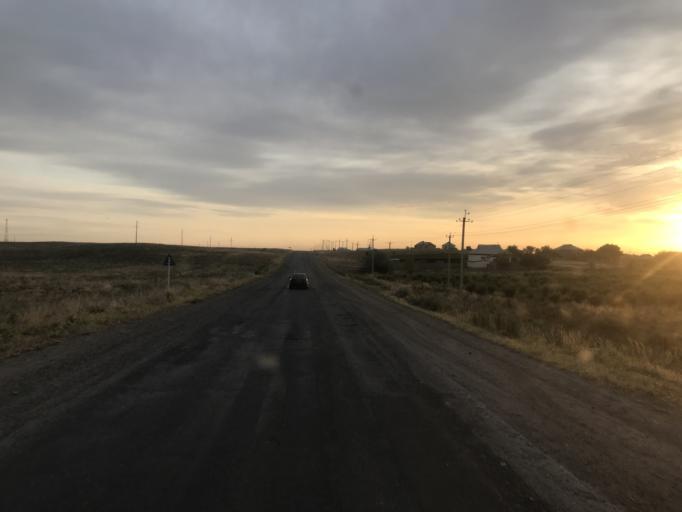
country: UZ
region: Toshkent
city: Amir Timur
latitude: 41.2334
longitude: 68.8102
